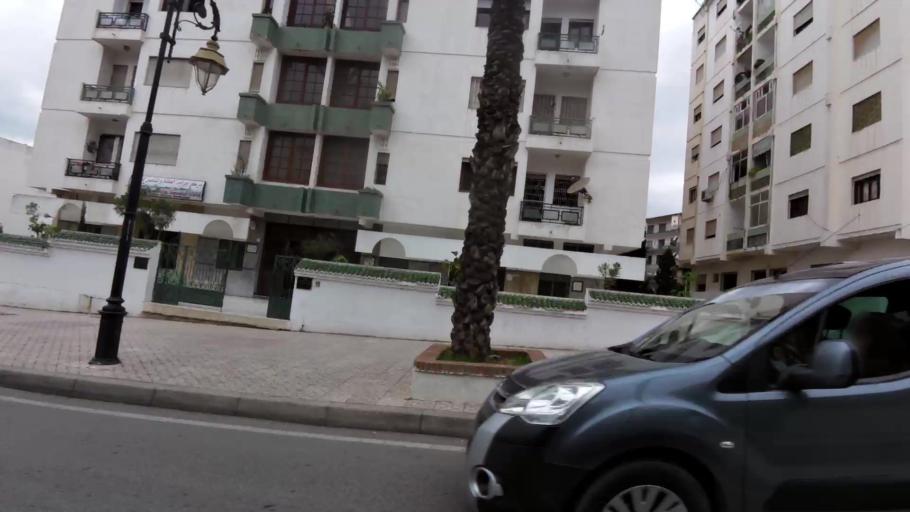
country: MA
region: Tanger-Tetouan
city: Tetouan
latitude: 35.5711
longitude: -5.3798
